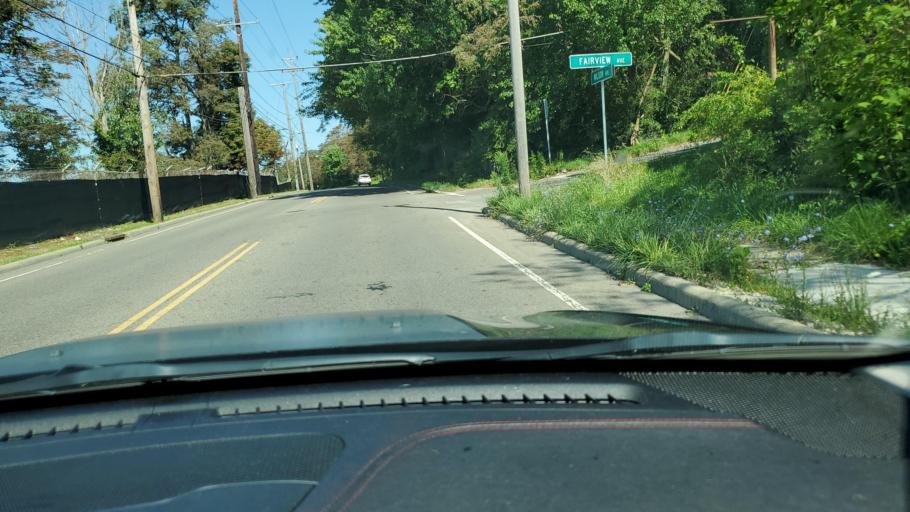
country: US
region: Ohio
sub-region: Mahoning County
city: Campbell
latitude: 41.0794
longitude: -80.6083
